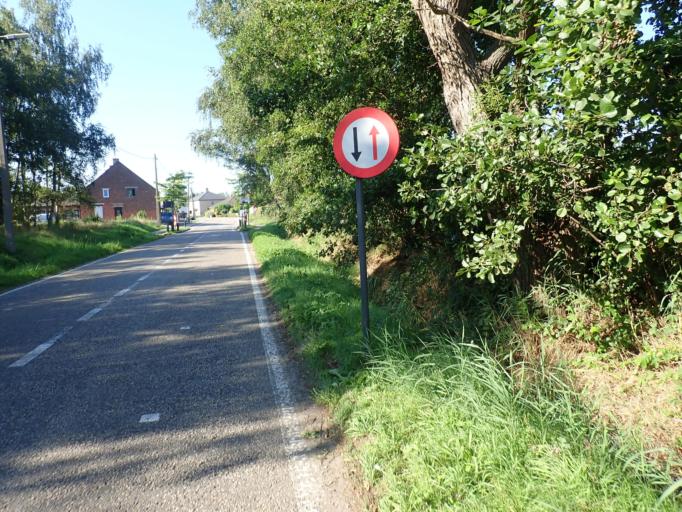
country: BE
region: Flanders
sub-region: Provincie Antwerpen
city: Herselt
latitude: 51.0568
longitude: 4.8420
